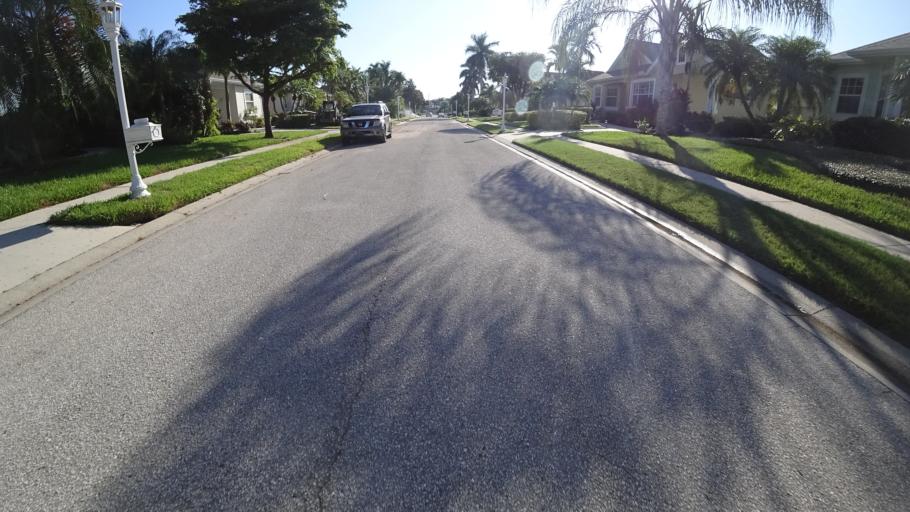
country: US
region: Florida
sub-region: Manatee County
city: Ellenton
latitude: 27.5029
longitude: -82.5082
